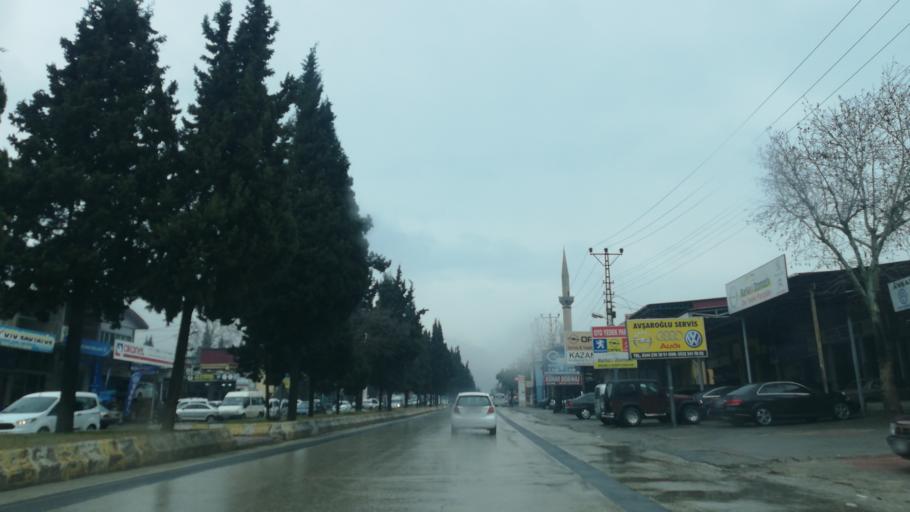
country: TR
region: Kahramanmaras
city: Kahramanmaras
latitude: 37.5620
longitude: 36.9570
